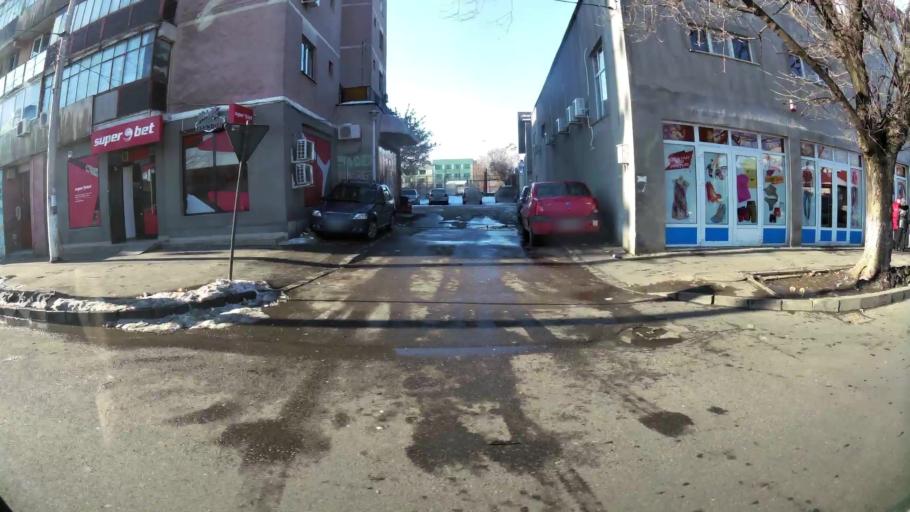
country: RO
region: Bucuresti
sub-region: Municipiul Bucuresti
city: Bucuresti
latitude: 44.3933
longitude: 26.0828
